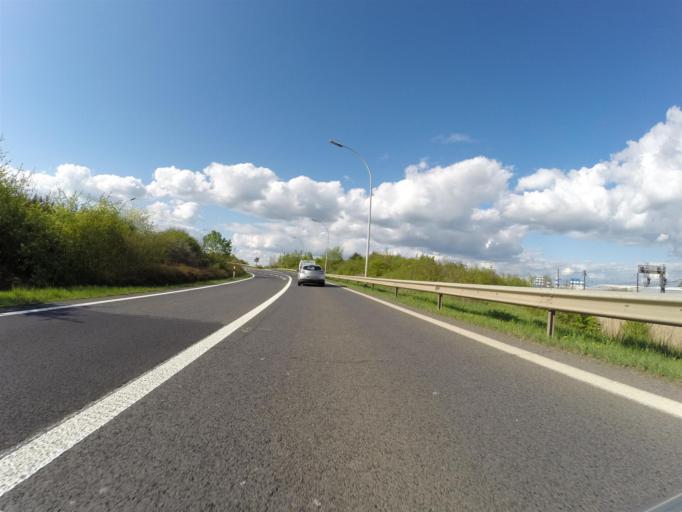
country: LU
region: Luxembourg
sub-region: Canton de Luxembourg
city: Hesperange
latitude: 49.5802
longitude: 6.1313
